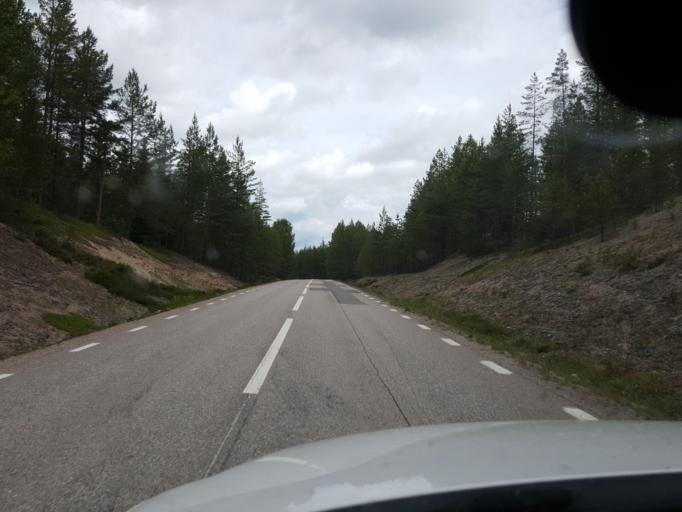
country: SE
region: Gaevleborg
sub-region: Ljusdals Kommun
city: Farila
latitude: 61.7888
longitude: 15.6373
